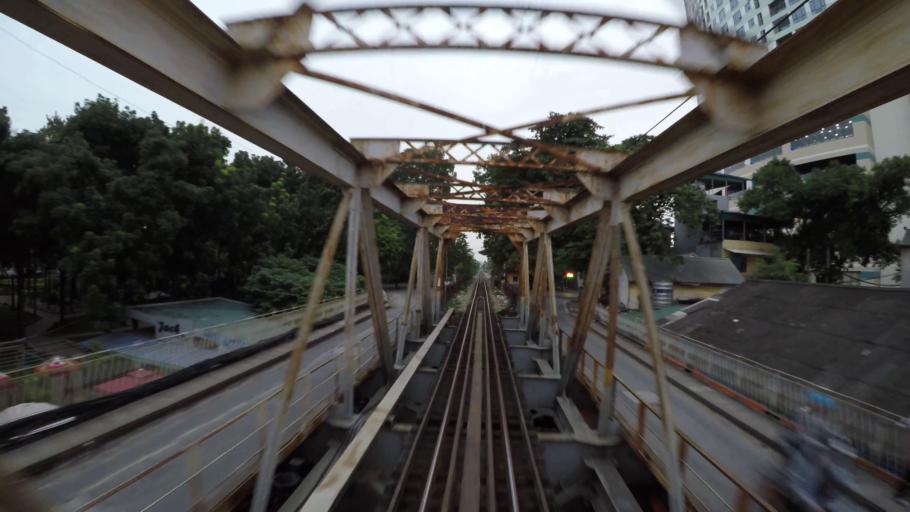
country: VN
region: Ha Noi
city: Hoan Kiem
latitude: 21.0501
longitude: 105.8916
